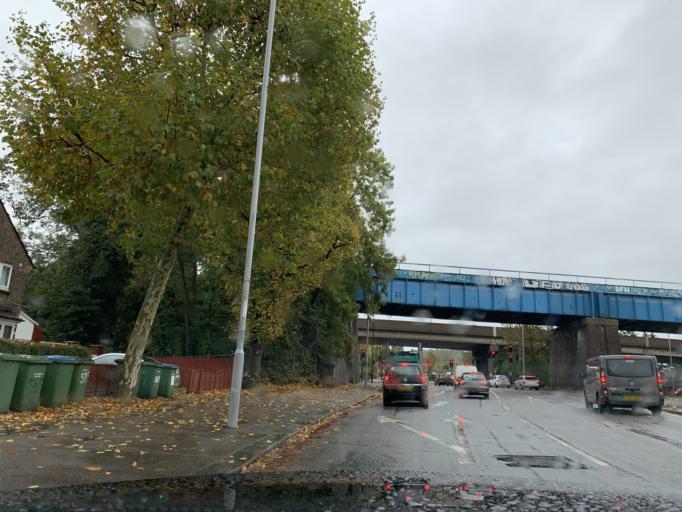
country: GB
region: England
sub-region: Greater London
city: Blackheath
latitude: 51.4565
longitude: 0.0413
